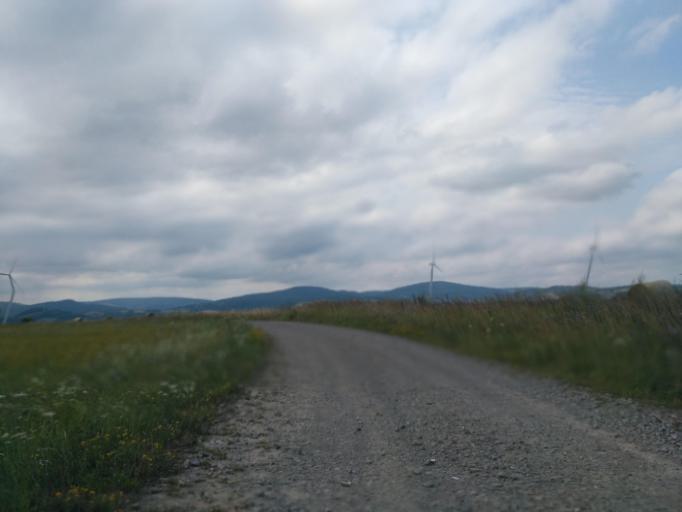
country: PL
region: Subcarpathian Voivodeship
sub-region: Powiat krosnienski
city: Rymanow
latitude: 49.6076
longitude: 21.8422
